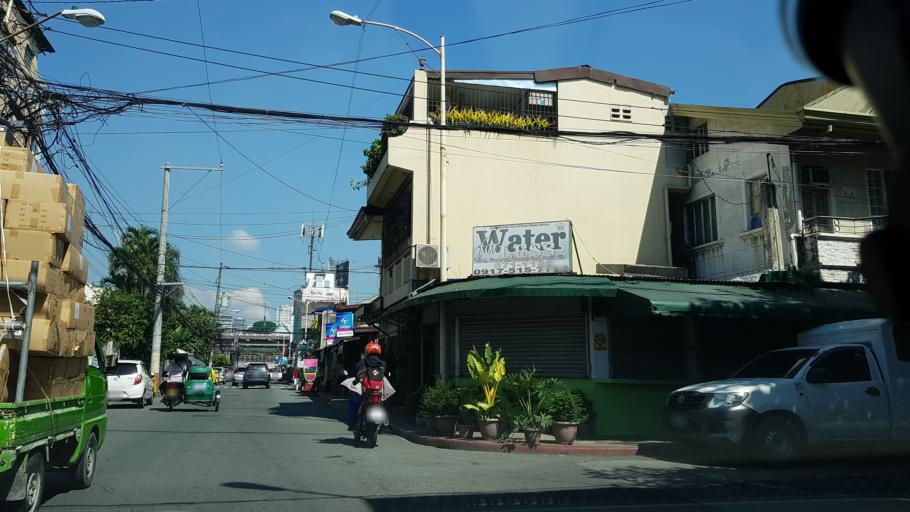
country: PH
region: Calabarzon
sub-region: Province of Rizal
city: Pateros
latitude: 14.5622
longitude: 121.0705
